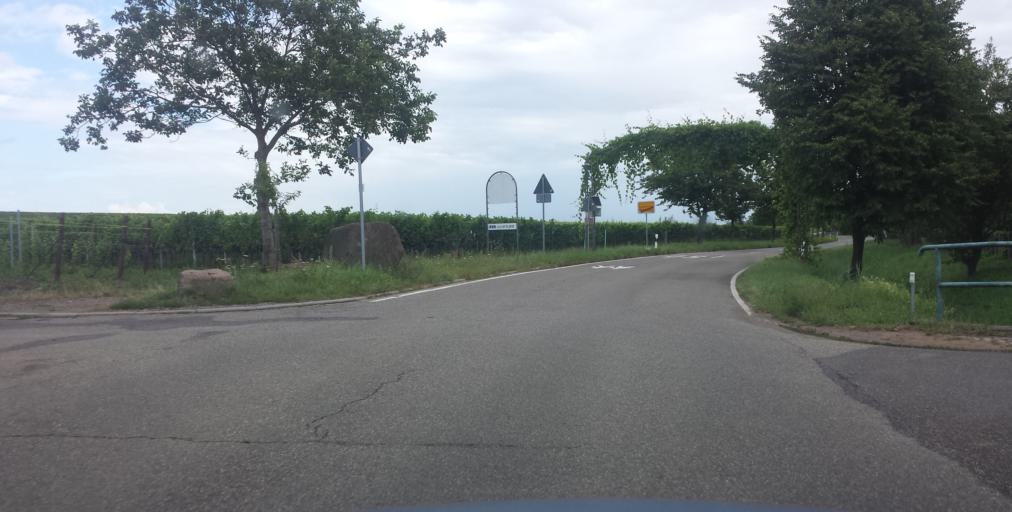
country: DE
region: Rheinland-Pfalz
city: Roschbach
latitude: 49.2476
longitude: 8.1227
